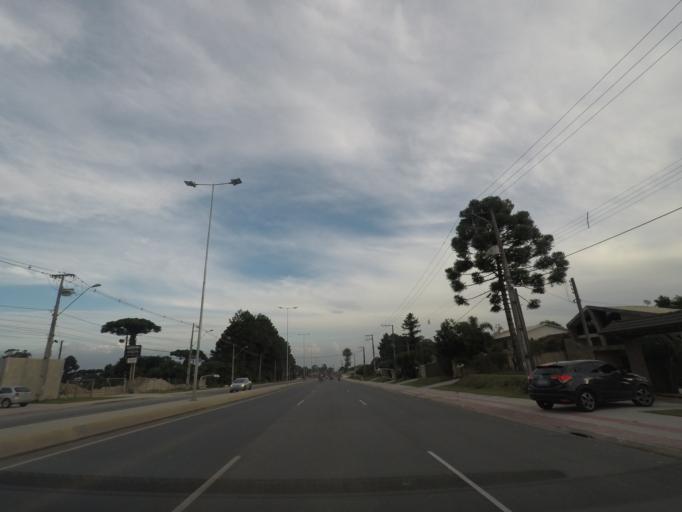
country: BR
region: Parana
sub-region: Colombo
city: Colombo
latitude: -25.3016
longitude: -49.2230
